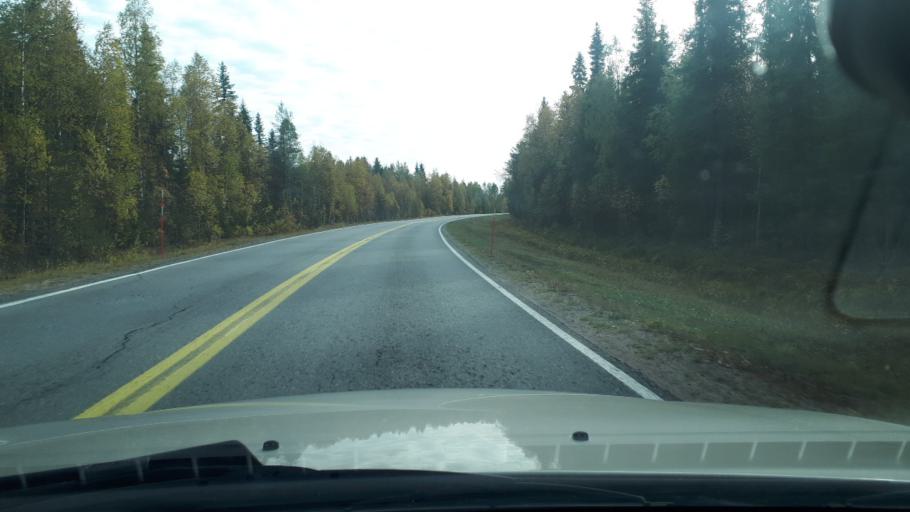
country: FI
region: Lapland
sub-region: Rovaniemi
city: Ranua
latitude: 65.9676
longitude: 26.0157
